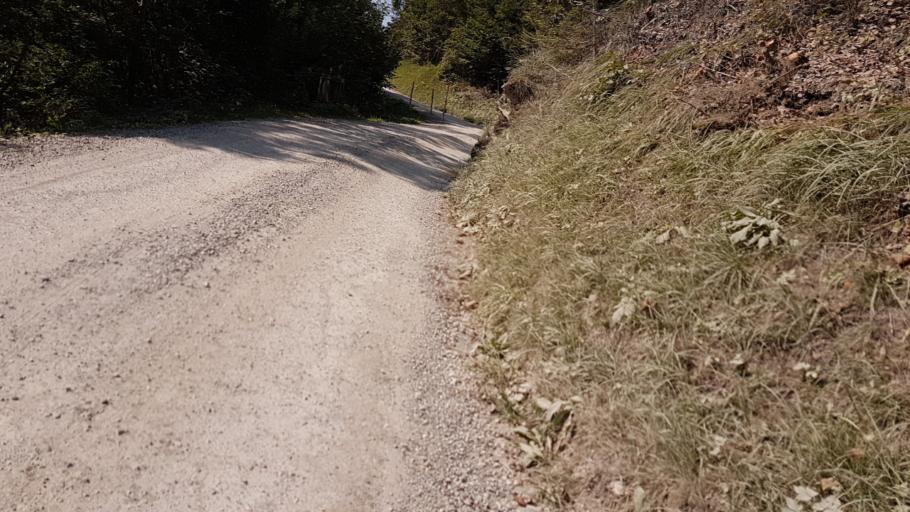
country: CH
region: Bern
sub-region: Frutigen-Niedersimmental District
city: Aeschi
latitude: 46.6324
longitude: 7.7419
